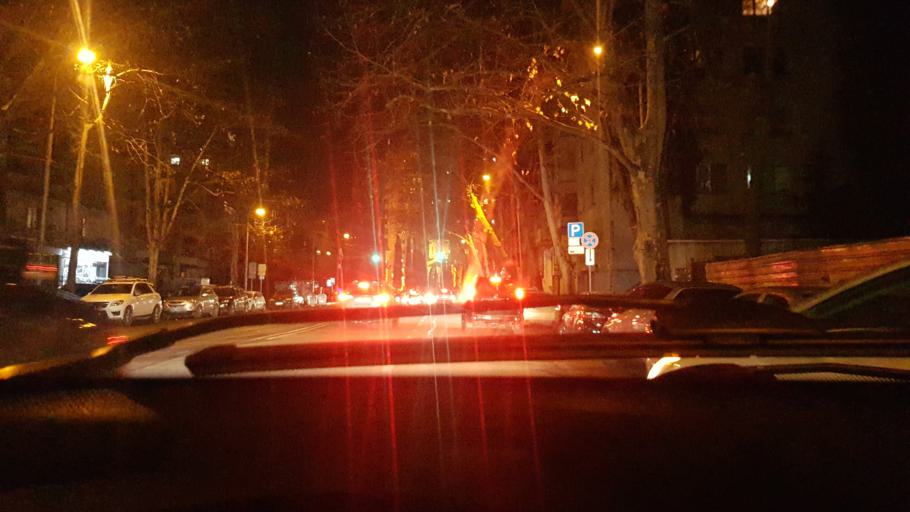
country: GE
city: Tsqnet'i
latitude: 41.7212
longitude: 44.7623
